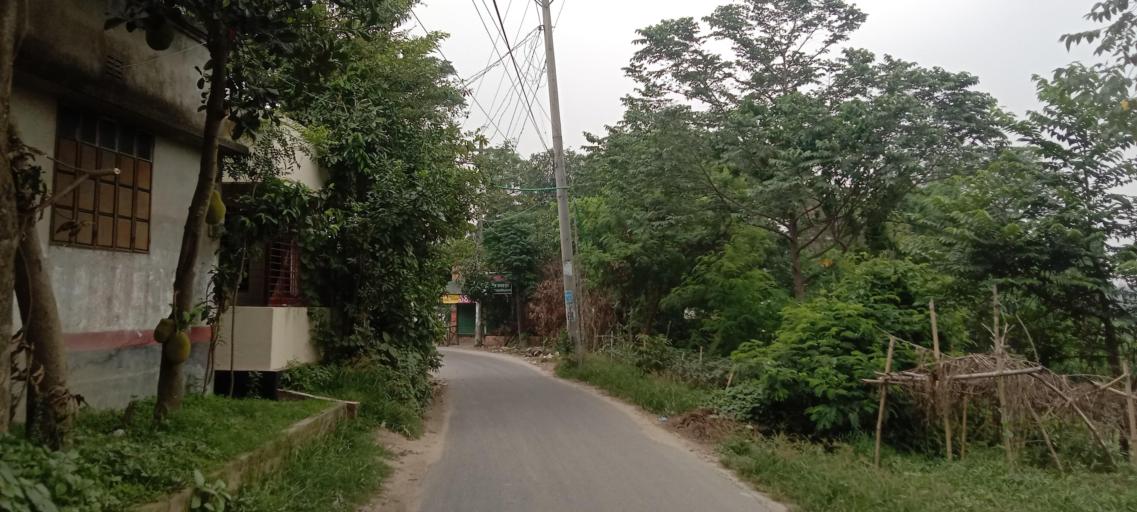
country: BD
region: Dhaka
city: Azimpur
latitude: 23.7450
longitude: 90.3095
